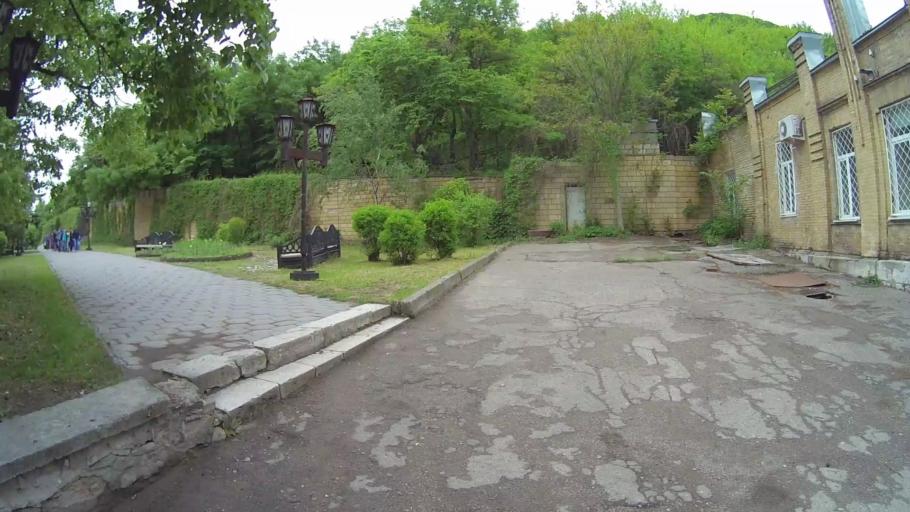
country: RU
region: Stavropol'skiy
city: Zheleznovodsk
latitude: 44.1349
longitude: 43.0266
